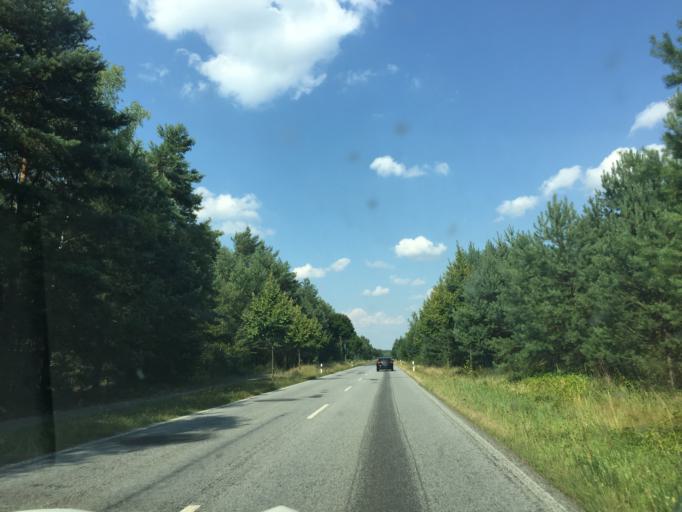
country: DE
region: Saxony
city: Schleife
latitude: 51.4687
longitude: 14.4913
